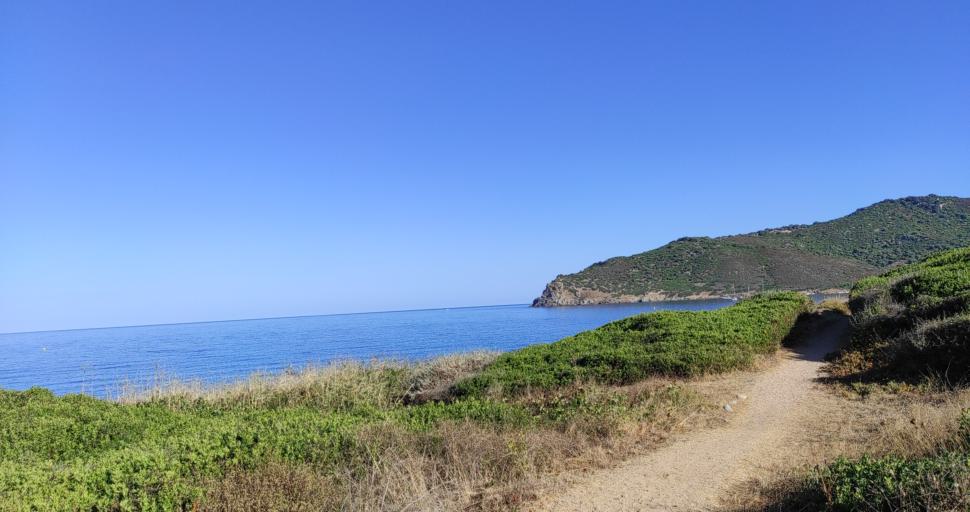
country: FR
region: Corsica
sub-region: Departement de la Corse-du-Sud
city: Alata
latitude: 41.9822
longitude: 8.6697
